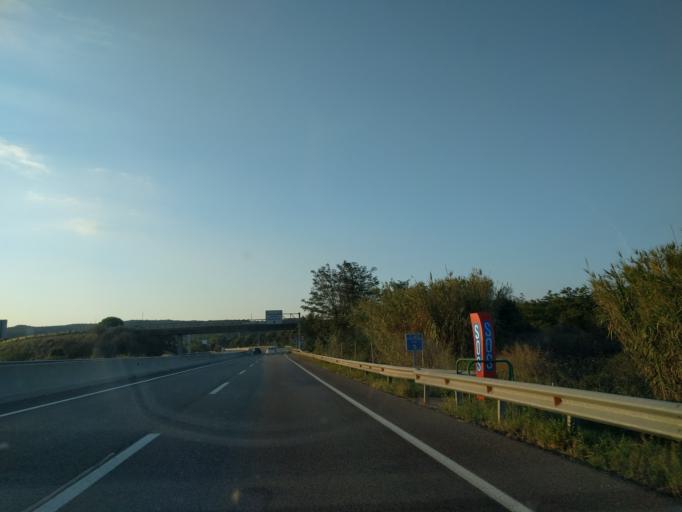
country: ES
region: Catalonia
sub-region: Provincia de Girona
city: Santa Cristina d'Aro
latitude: 41.8217
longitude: 2.9773
